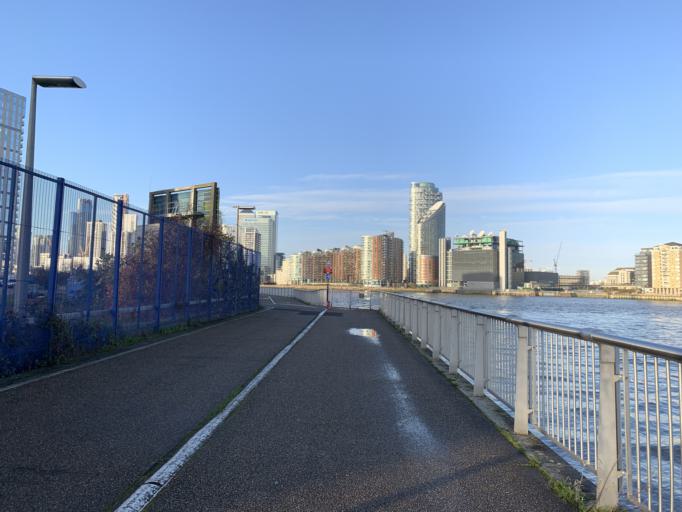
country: GB
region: England
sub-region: Greater London
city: Poplar
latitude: 51.5049
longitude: 0.0036
